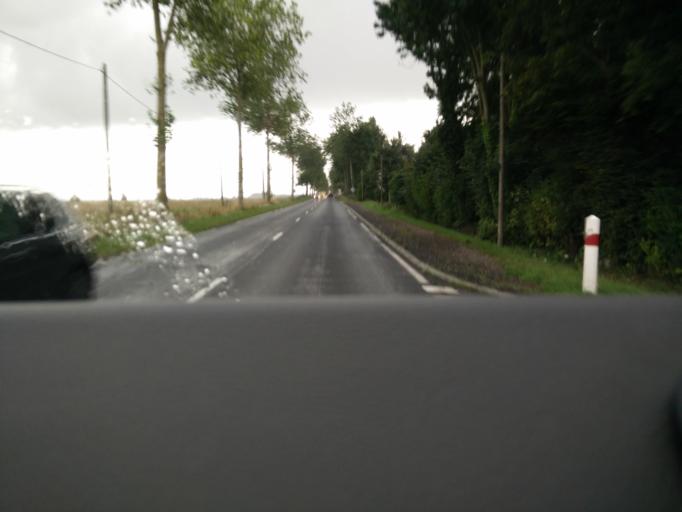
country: FR
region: Nord-Pas-de-Calais
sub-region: Departement du Pas-de-Calais
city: Savy-Berlette
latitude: 50.3502
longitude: 2.5281
